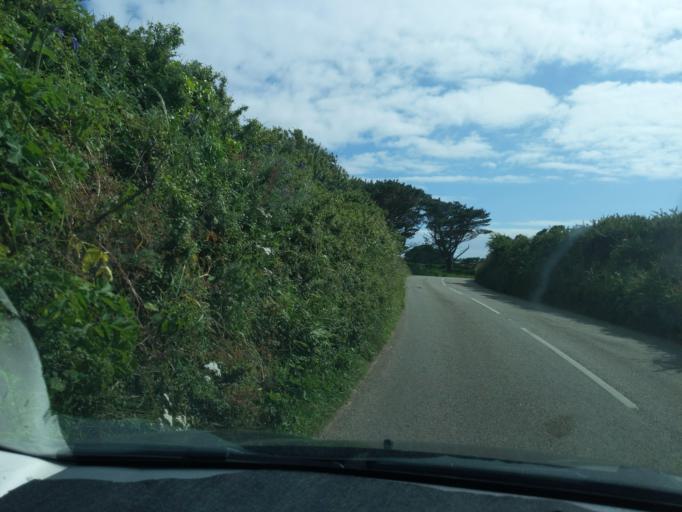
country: GB
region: England
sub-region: Cornwall
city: St. Buryan
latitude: 50.0635
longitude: -5.6348
